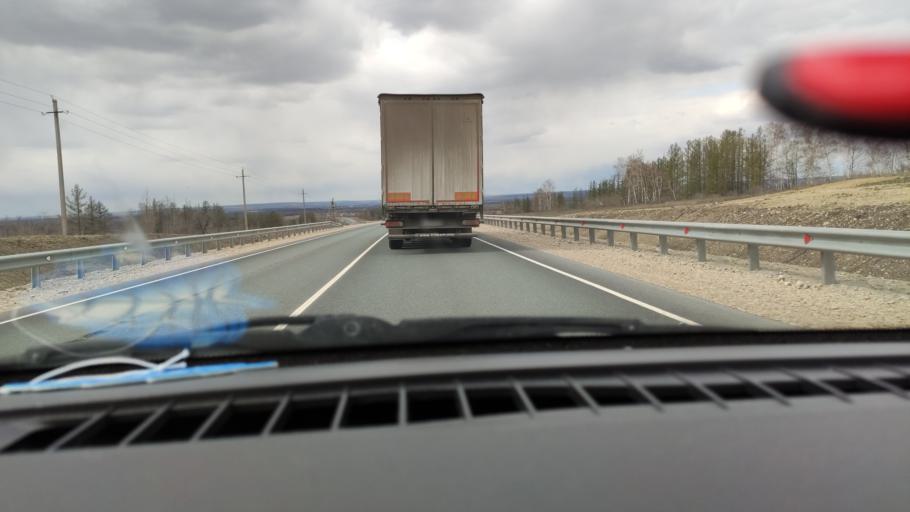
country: RU
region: Saratov
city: Shikhany
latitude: 52.1612
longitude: 47.1037
